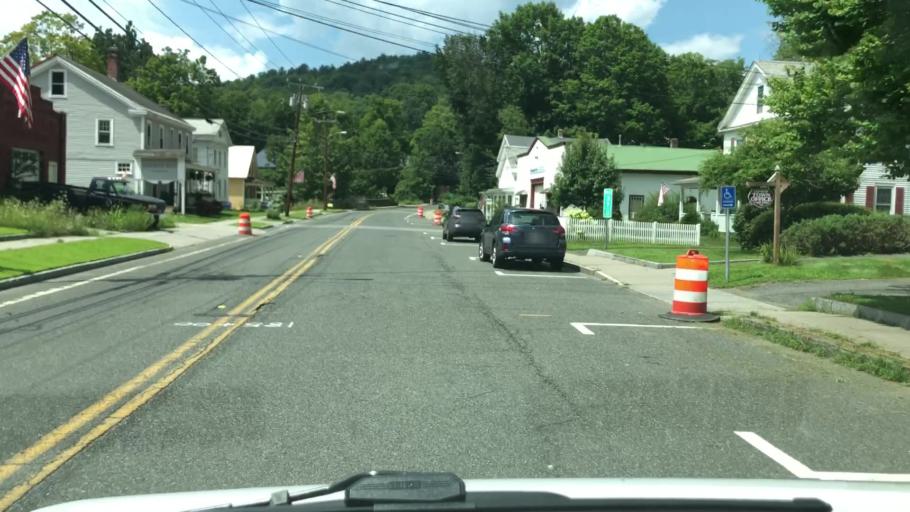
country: US
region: Massachusetts
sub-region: Franklin County
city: Conway
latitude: 42.5086
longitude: -72.6967
